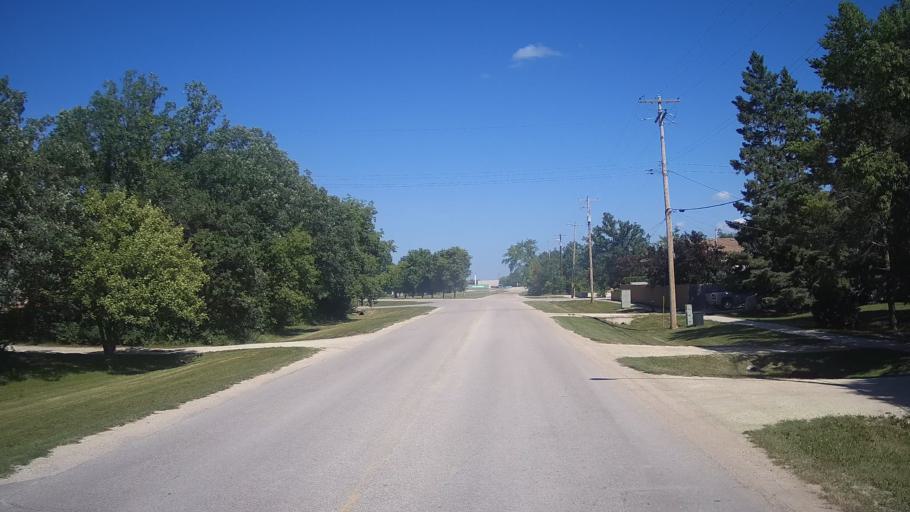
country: CA
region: Manitoba
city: Stonewall
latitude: 50.1304
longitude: -97.3321
